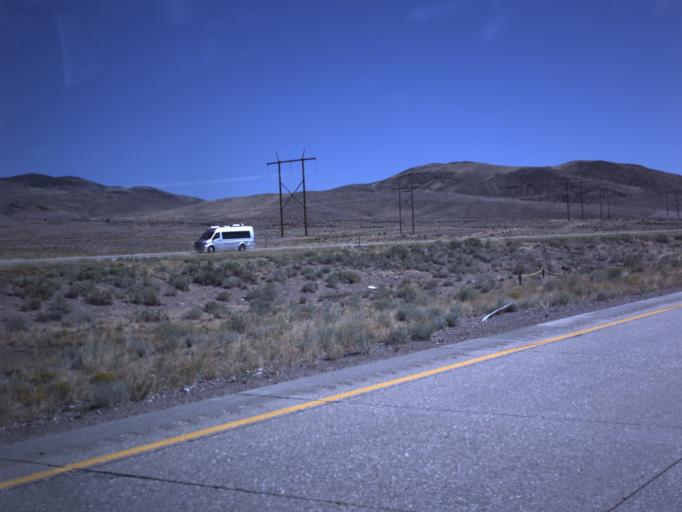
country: US
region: Utah
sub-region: Sevier County
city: Monroe
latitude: 38.6577
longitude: -112.2002
